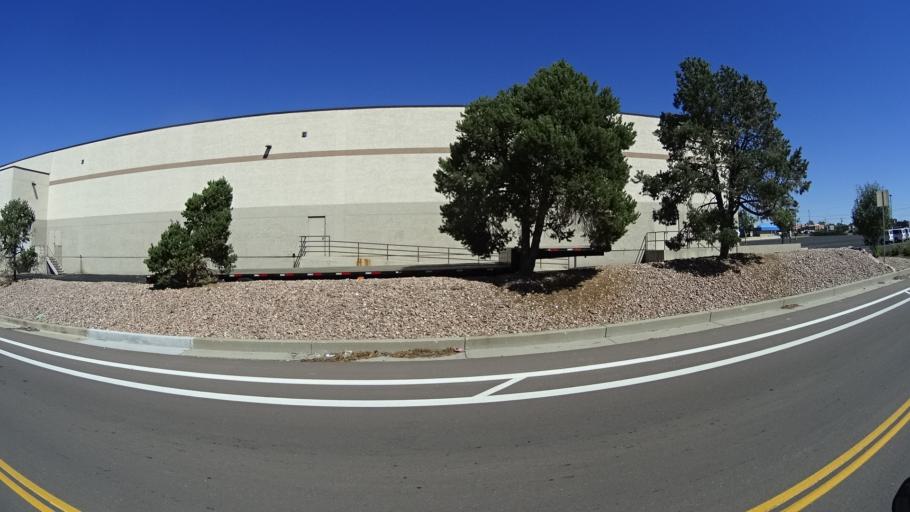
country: US
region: Colorado
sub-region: El Paso County
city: Stratmoor
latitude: 38.7871
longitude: -104.7604
